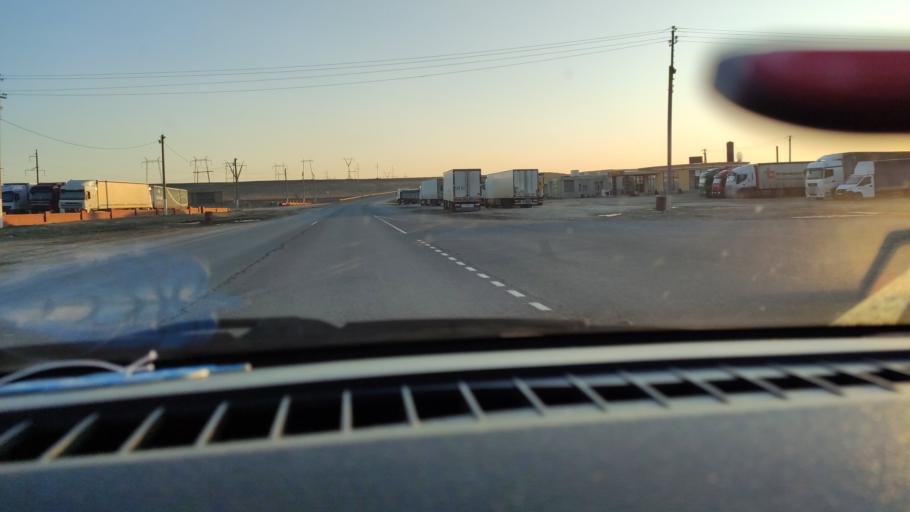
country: RU
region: Saratov
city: Sinodskoye
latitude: 51.9225
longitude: 46.5622
